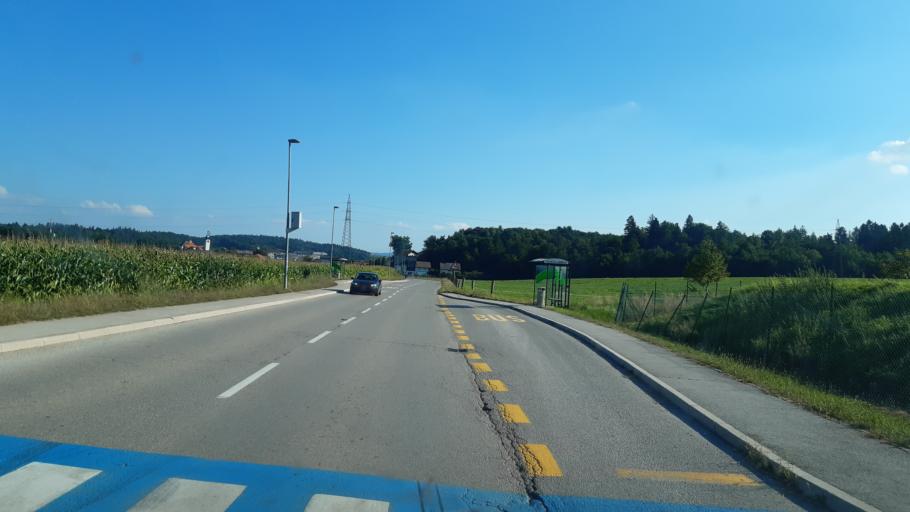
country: SI
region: Ivancna Gorica
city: Ivancna Gorica
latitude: 45.9455
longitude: 14.8033
